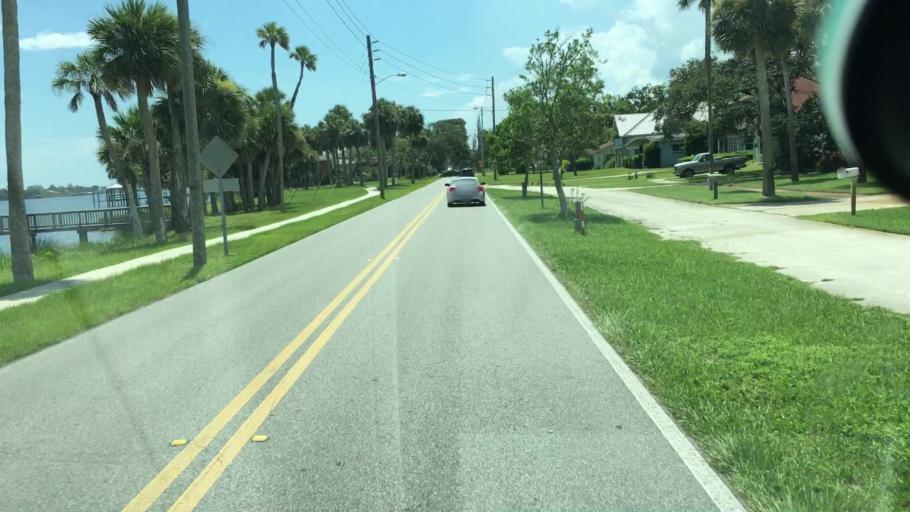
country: US
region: Florida
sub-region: Volusia County
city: Holly Hill
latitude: 29.2614
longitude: -81.0433
